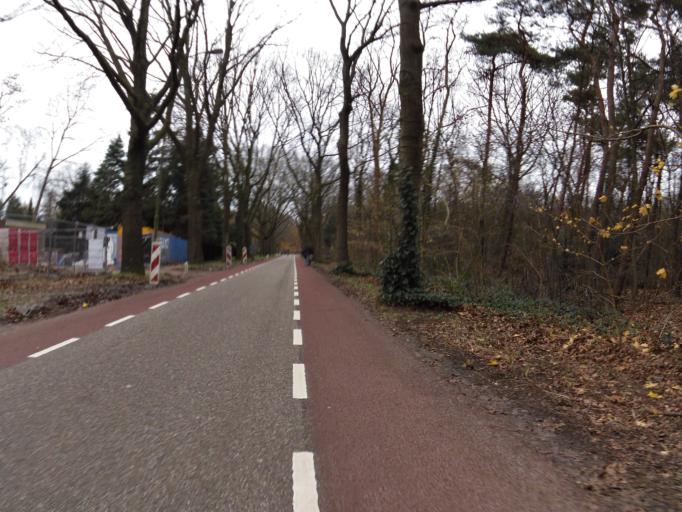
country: NL
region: North Brabant
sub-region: Gemeente Bernheze
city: Heesch
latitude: 51.7514
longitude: 5.5455
